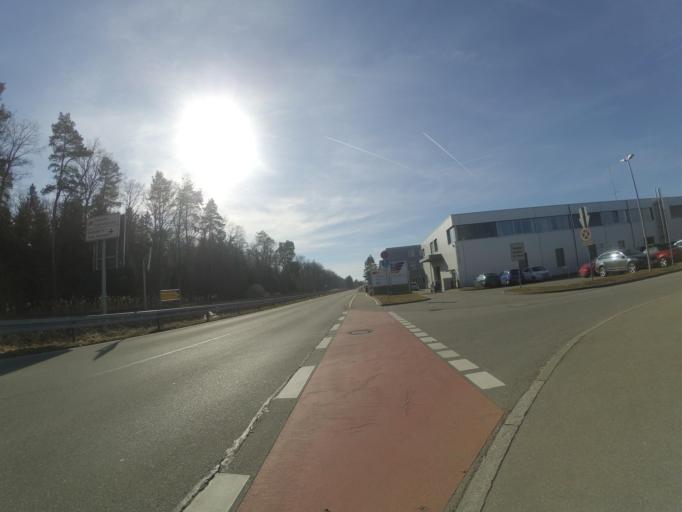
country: DE
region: Baden-Wuerttemberg
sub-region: Tuebingen Region
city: Friedrichshafen
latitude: 47.6717
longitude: 9.5221
